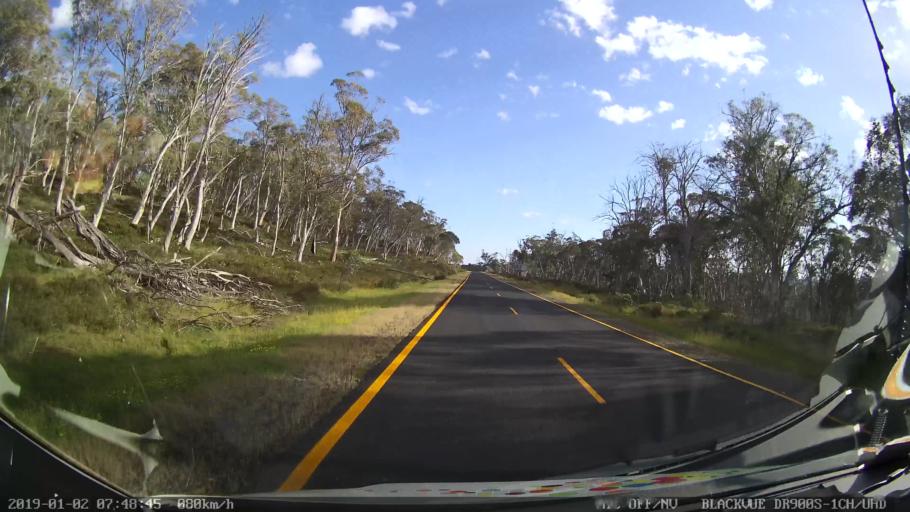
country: AU
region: New South Wales
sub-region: Tumut Shire
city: Tumut
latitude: -35.7494
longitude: 148.5196
